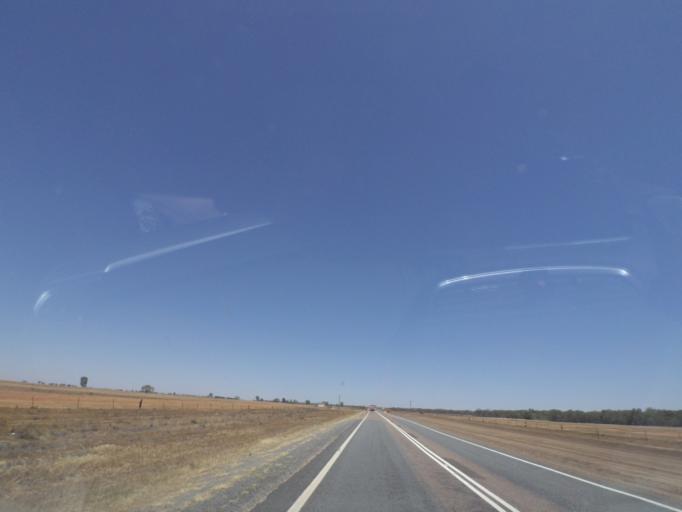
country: AU
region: New South Wales
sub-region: Berrigan
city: Berrigan
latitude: -35.1495
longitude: 145.9944
